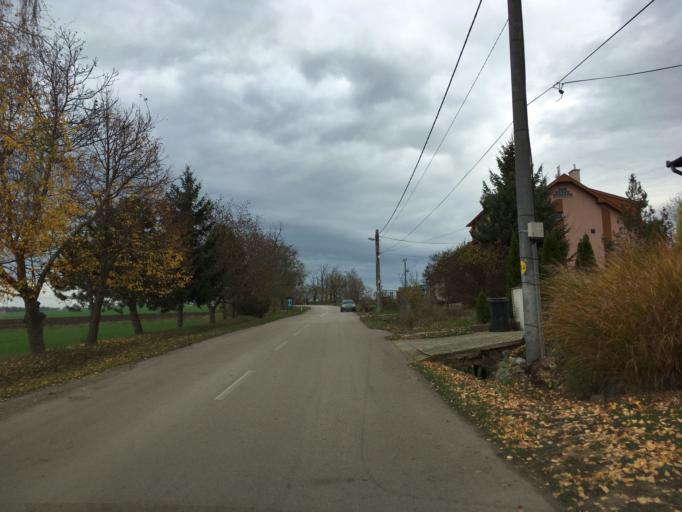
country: SK
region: Nitriansky
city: Svodin
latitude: 48.0219
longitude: 18.4070
